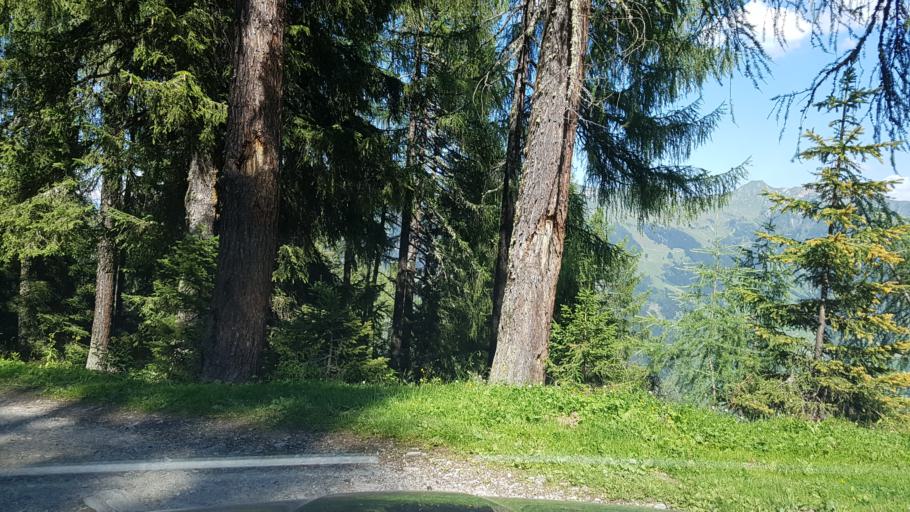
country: AT
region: Salzburg
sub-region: Politischer Bezirk Sankt Johann im Pongau
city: Dorfgastein
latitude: 47.2414
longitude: 13.0701
